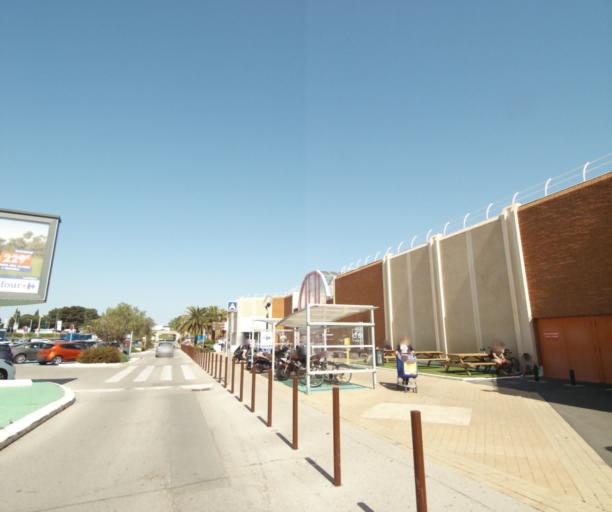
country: FR
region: Languedoc-Roussillon
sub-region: Departement de l'Herault
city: Lattes
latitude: 43.5826
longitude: 3.9277
